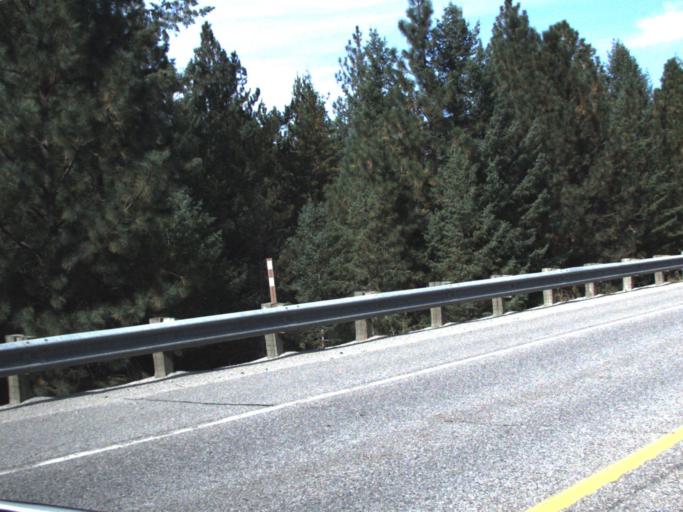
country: US
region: Washington
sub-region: Stevens County
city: Chewelah
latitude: 48.1509
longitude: -117.6887
